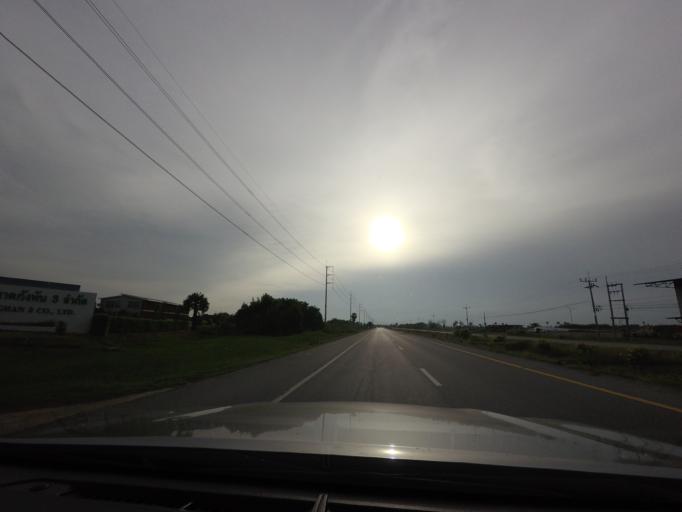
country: TH
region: Nakhon Si Thammarat
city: Hua Sai
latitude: 7.9956
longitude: 100.3176
